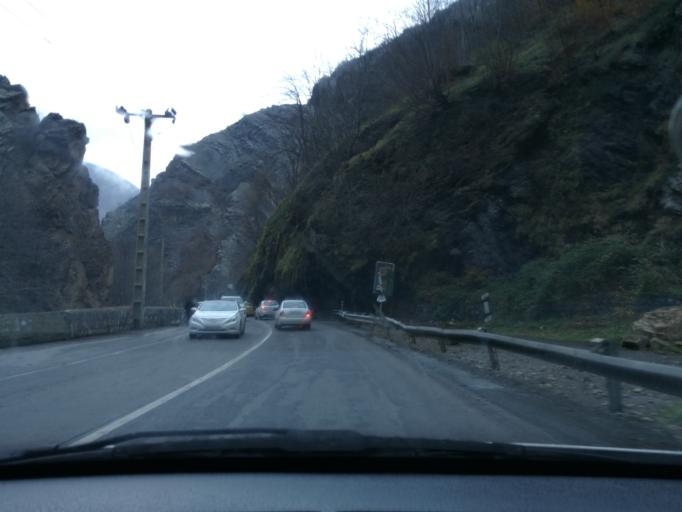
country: IR
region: Mazandaran
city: Chalus
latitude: 36.2762
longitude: 51.2443
